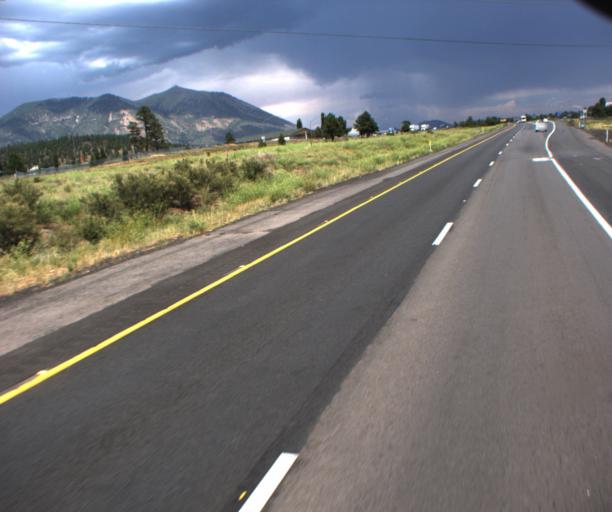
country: US
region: Arizona
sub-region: Coconino County
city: Flagstaff
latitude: 35.1882
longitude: -111.6272
